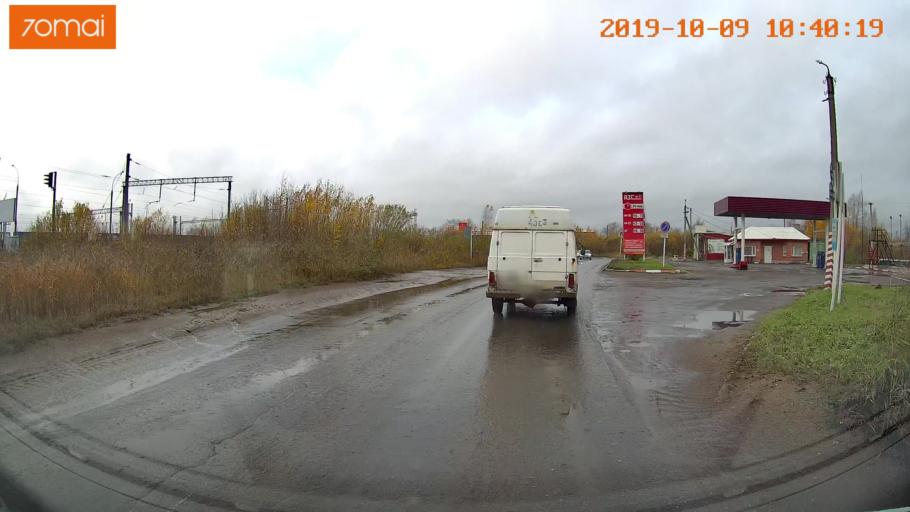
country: RU
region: Vologda
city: Vologda
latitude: 59.2335
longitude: 39.8378
